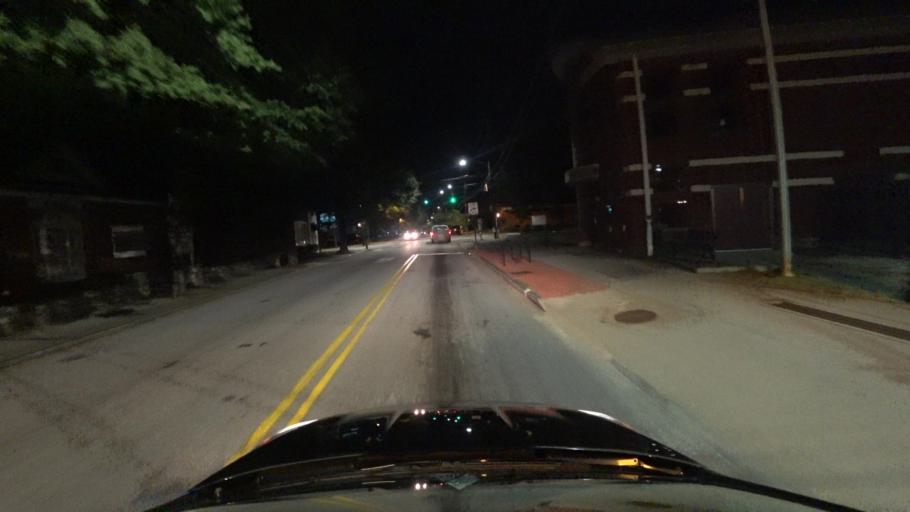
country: US
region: Georgia
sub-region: DeKalb County
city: Druid Hills
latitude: 33.7424
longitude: -84.3478
